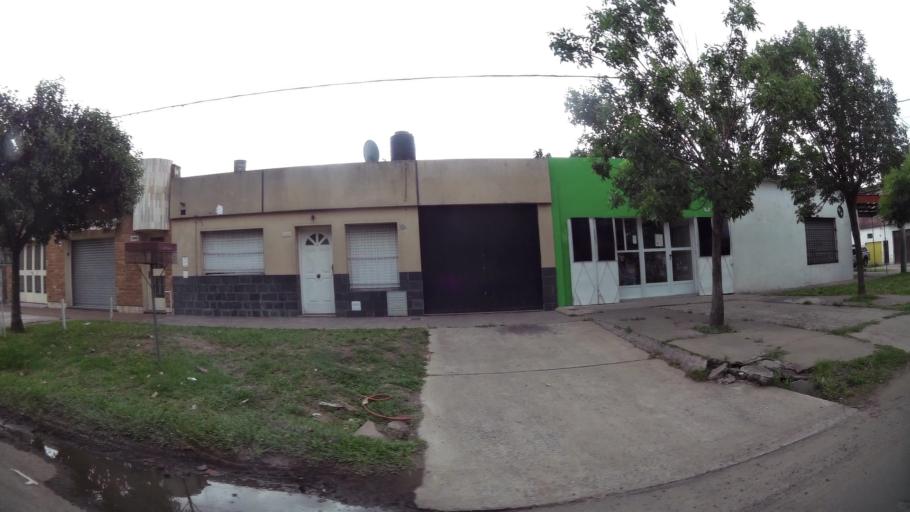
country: AR
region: Santa Fe
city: Gobernador Galvez
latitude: -33.0013
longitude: -60.6779
